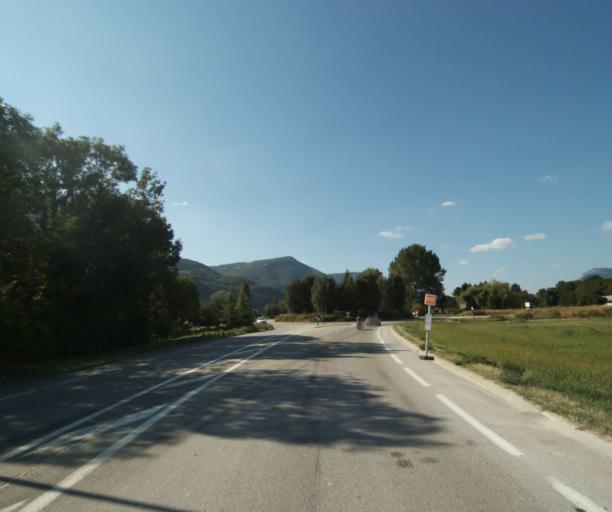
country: FR
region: Rhone-Alpes
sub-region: Departement de l'Isere
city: Fontanil-Cornillon
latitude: 45.2304
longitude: 5.6480
